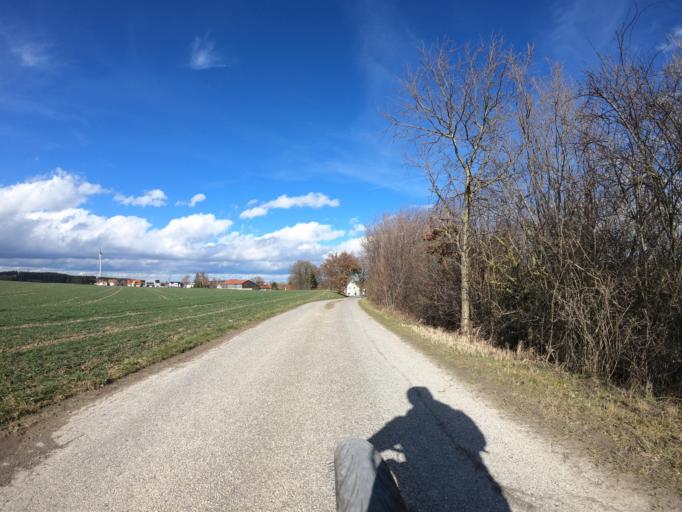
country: DE
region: Bavaria
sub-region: Upper Bavaria
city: Landsberied
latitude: 48.1779
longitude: 11.1830
